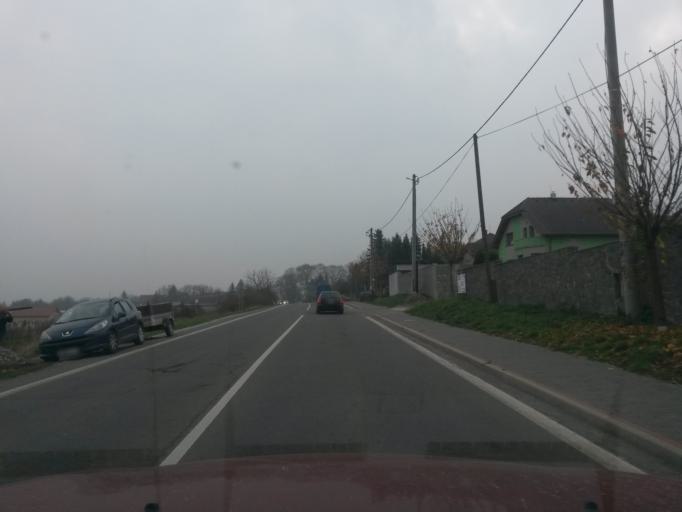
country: SK
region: Kosicky
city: Kosice
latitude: 48.8044
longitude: 21.3020
